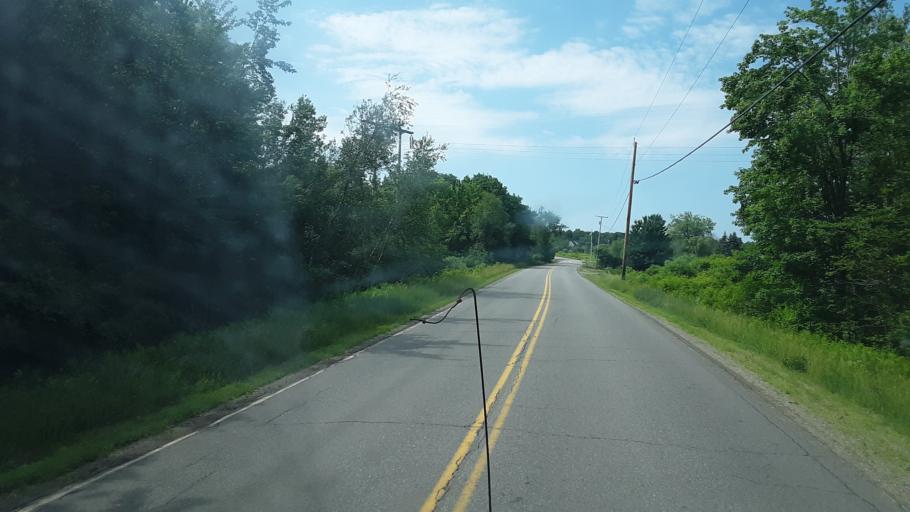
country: US
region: Maine
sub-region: Waldo County
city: Frankfort
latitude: 44.5950
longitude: -68.9429
